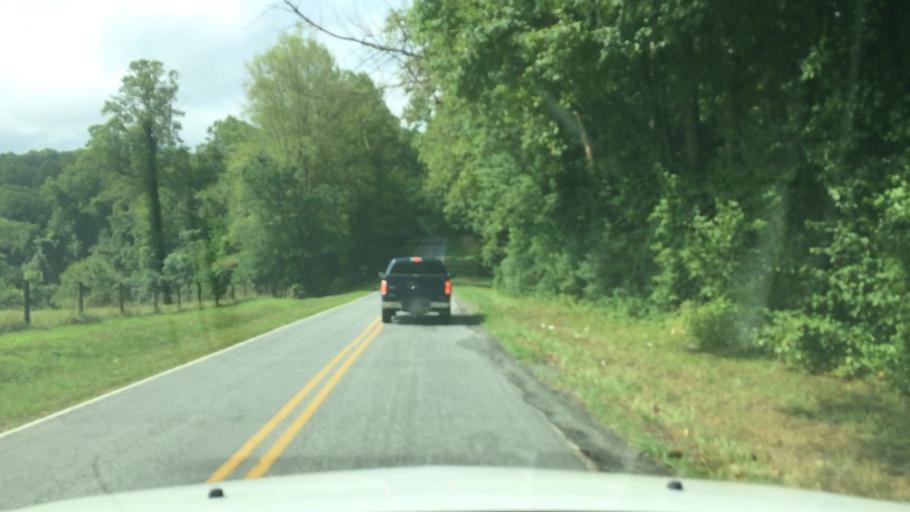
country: US
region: North Carolina
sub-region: Yadkin County
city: Jonesville
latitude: 36.1095
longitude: -80.8566
